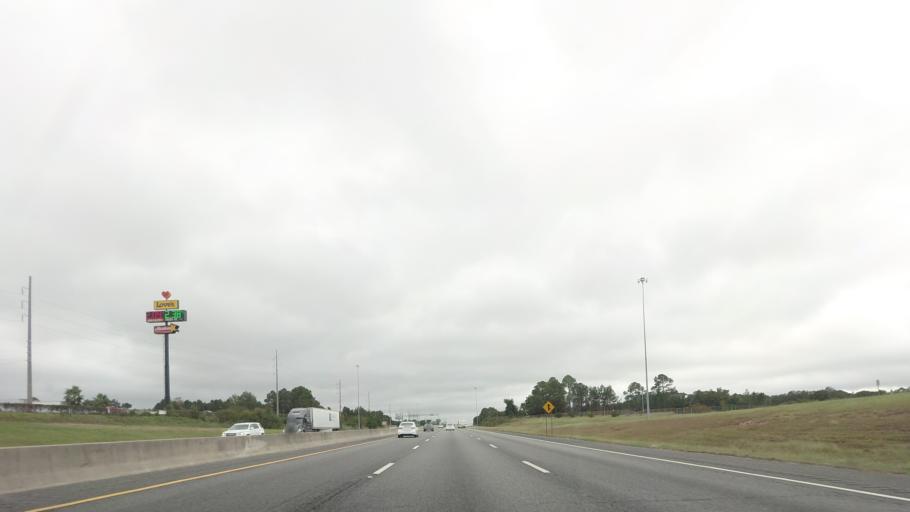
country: US
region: Georgia
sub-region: Tift County
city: Unionville
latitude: 31.4154
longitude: -83.5050
